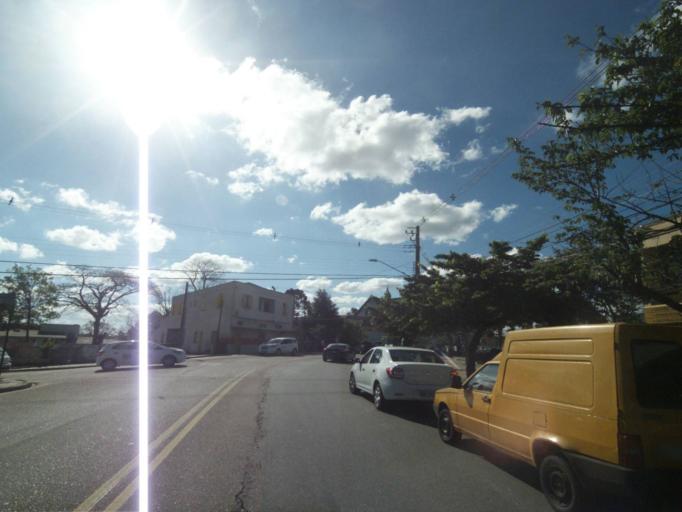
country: BR
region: Parana
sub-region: Curitiba
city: Curitiba
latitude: -25.3929
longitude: -49.2606
